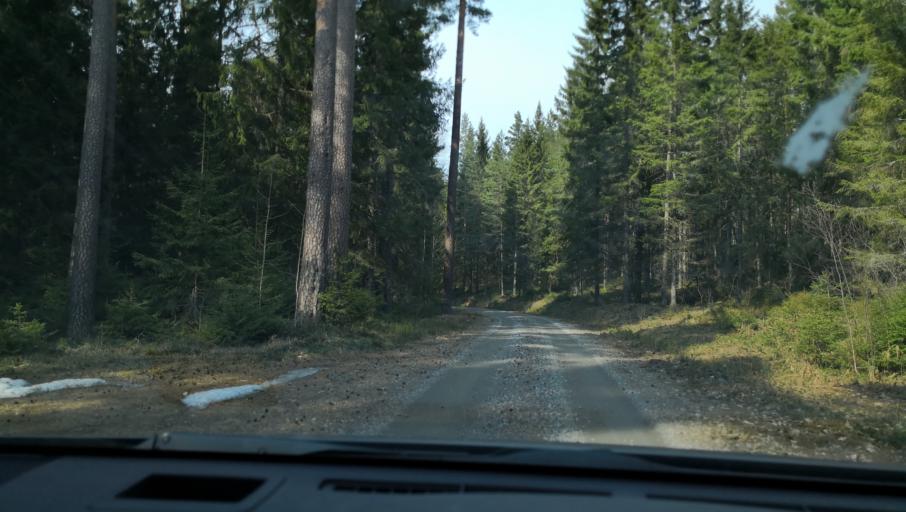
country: SE
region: OErebro
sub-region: Lindesbergs Kommun
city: Frovi
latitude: 59.3782
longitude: 15.4192
